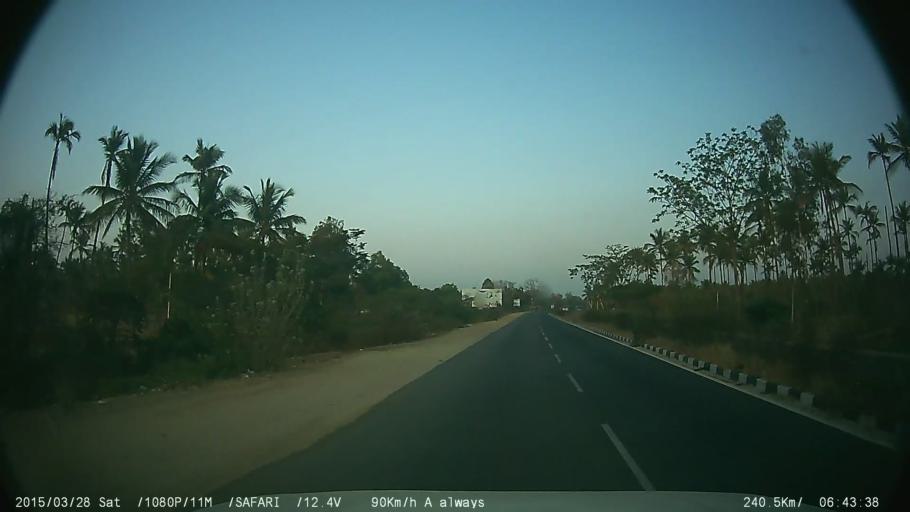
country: IN
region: Karnataka
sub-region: Mandya
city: Maddur
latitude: 12.6312
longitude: 77.1167
